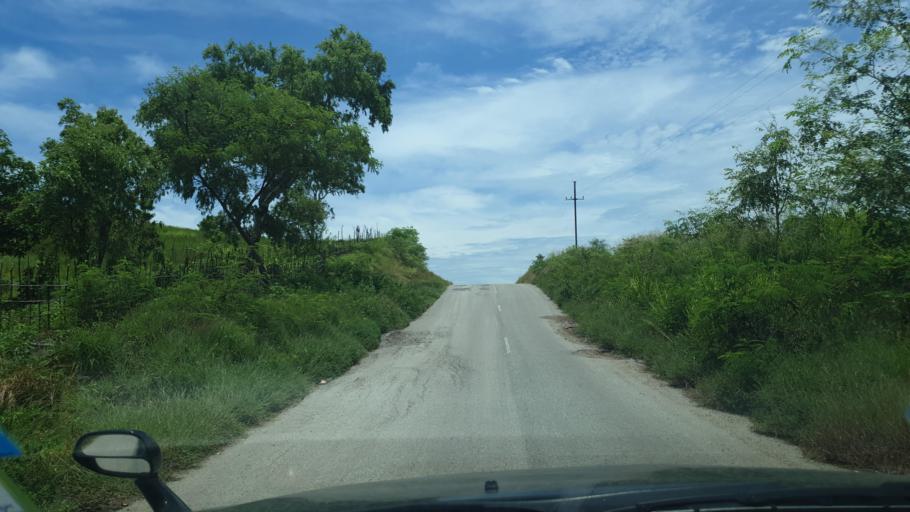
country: PG
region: National Capital
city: Port Moresby
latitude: -9.4263
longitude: 147.0513
